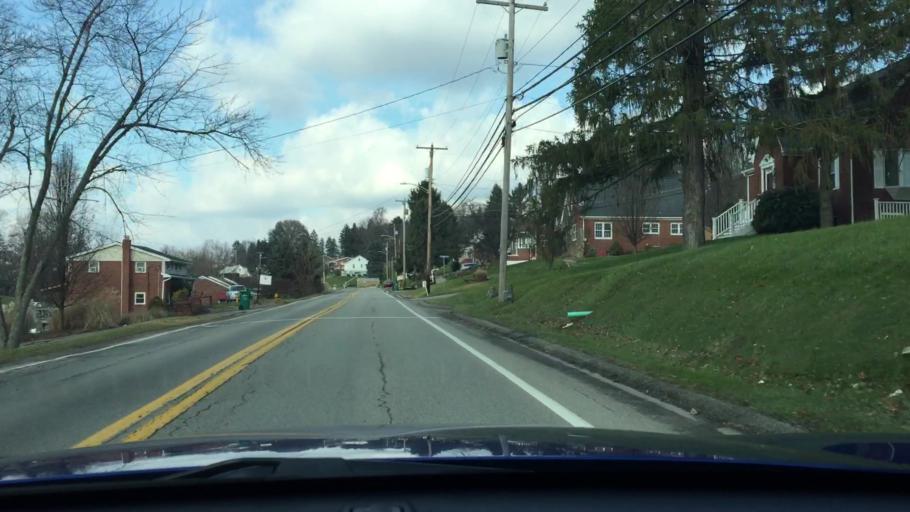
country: US
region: Pennsylvania
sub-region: Washington County
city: Canonsburg
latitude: 40.2591
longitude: -80.1594
